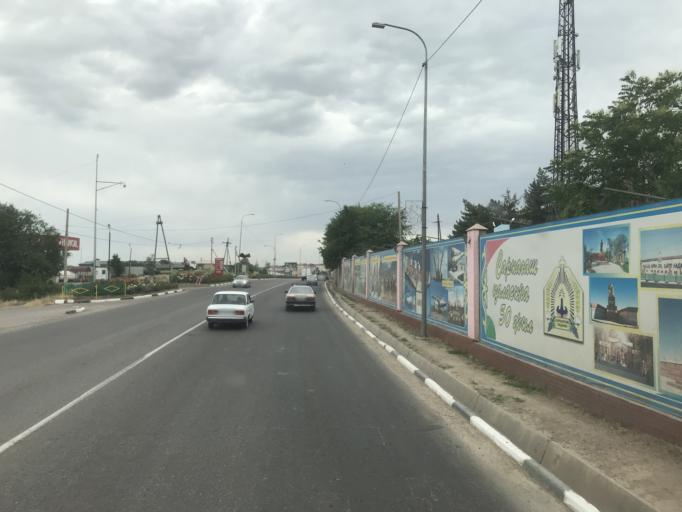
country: KZ
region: Ongtustik Qazaqstan
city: Saryaghash
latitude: 41.4696
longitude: 69.1752
